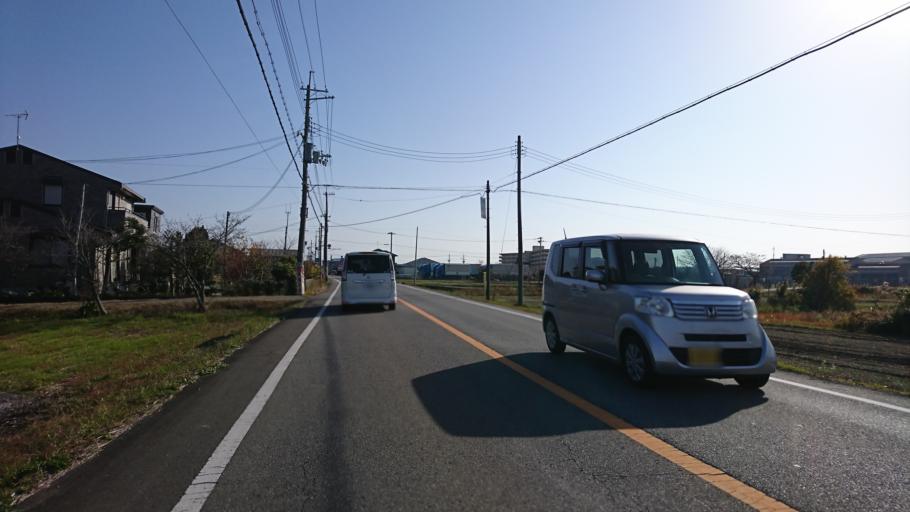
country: JP
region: Hyogo
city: Miki
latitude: 34.7618
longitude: 134.9125
